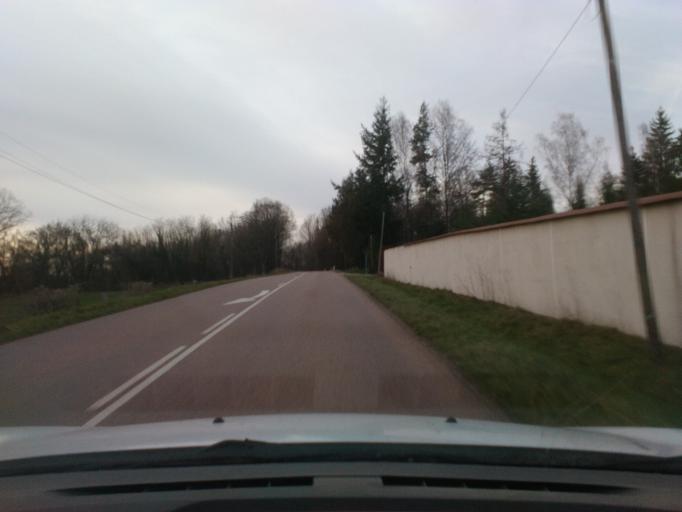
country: FR
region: Lorraine
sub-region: Departement des Vosges
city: Portieux
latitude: 48.3541
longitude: 6.3345
